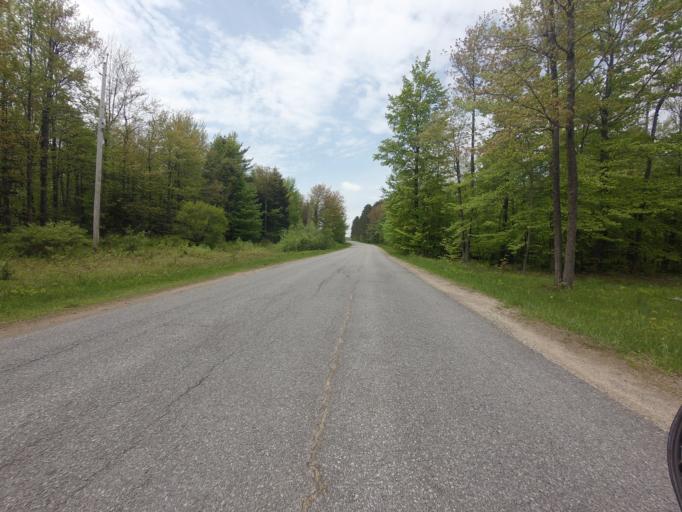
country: US
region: New York
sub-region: St. Lawrence County
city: Hannawa Falls
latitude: 44.5531
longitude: -74.9544
